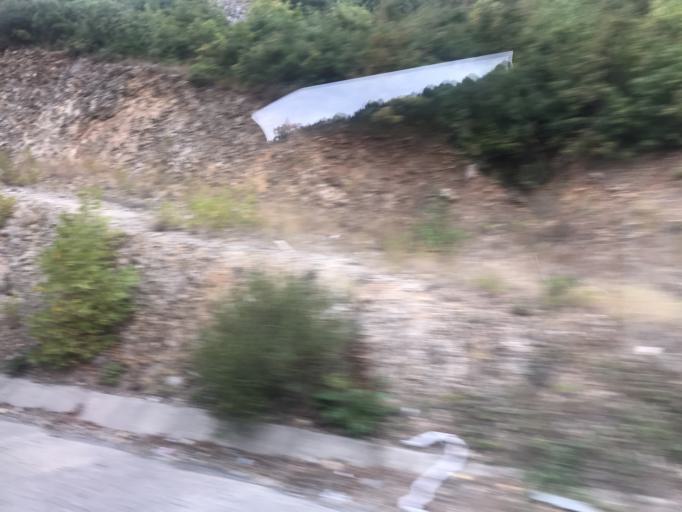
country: TR
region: Balikesir
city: Ergama
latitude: 39.6274
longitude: 27.6113
